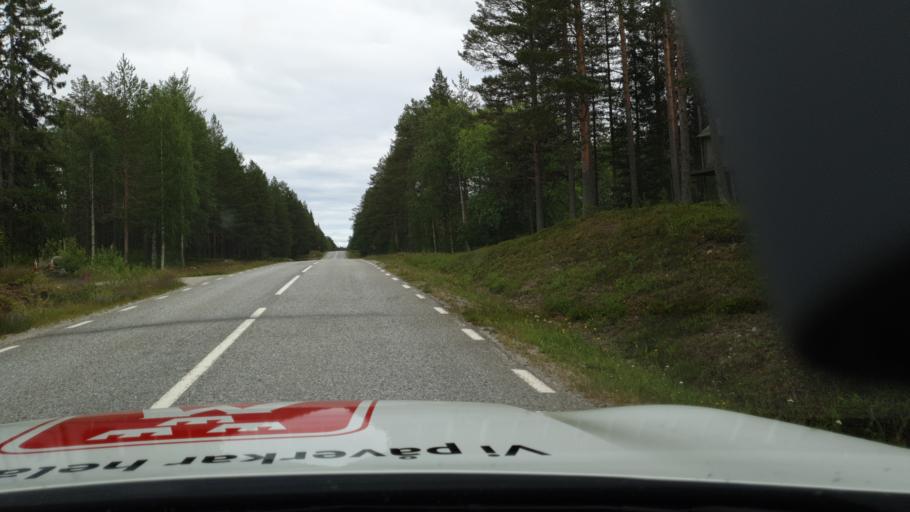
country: SE
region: Vaesterbotten
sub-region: Lycksele Kommun
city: Soderfors
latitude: 64.6257
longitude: 18.0738
